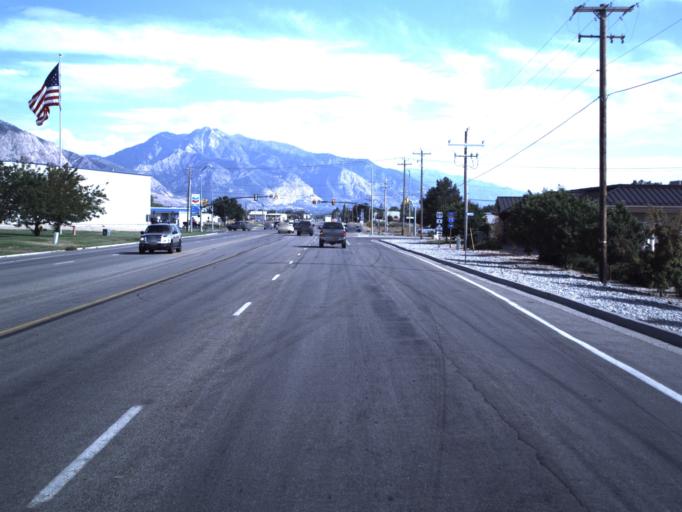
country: US
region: Utah
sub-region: Weber County
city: Pleasant View
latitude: 41.3082
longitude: -112.0069
